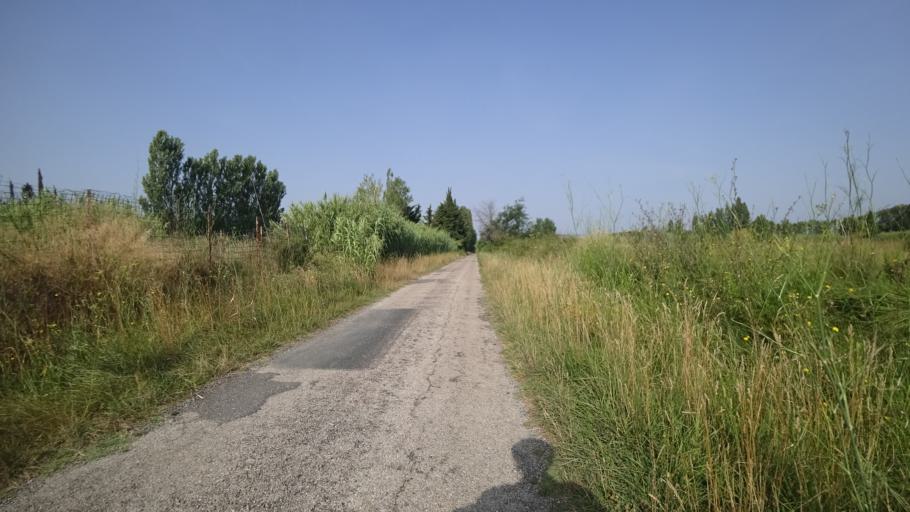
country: FR
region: Languedoc-Roussillon
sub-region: Departement des Pyrenees-Orientales
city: Villelongue-de-la-Salanque
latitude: 42.7346
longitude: 3.0022
